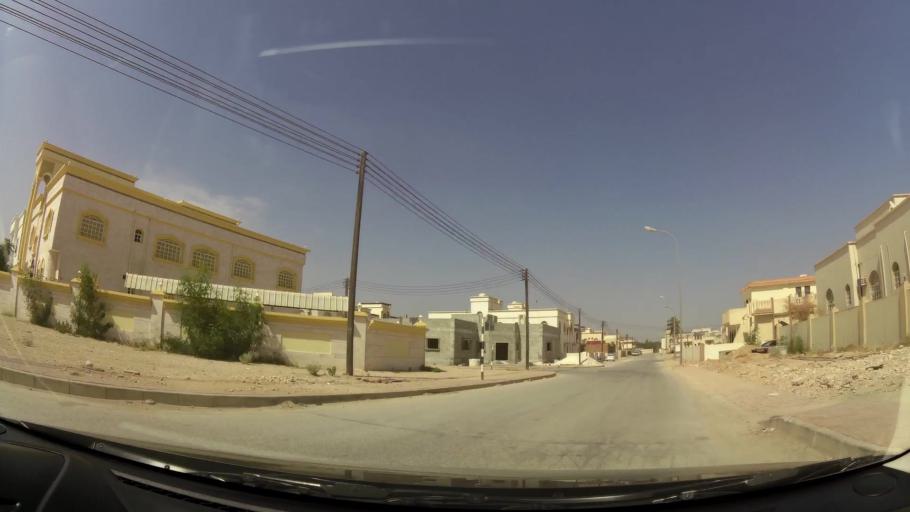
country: OM
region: Zufar
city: Salalah
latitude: 17.0446
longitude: 54.1578
